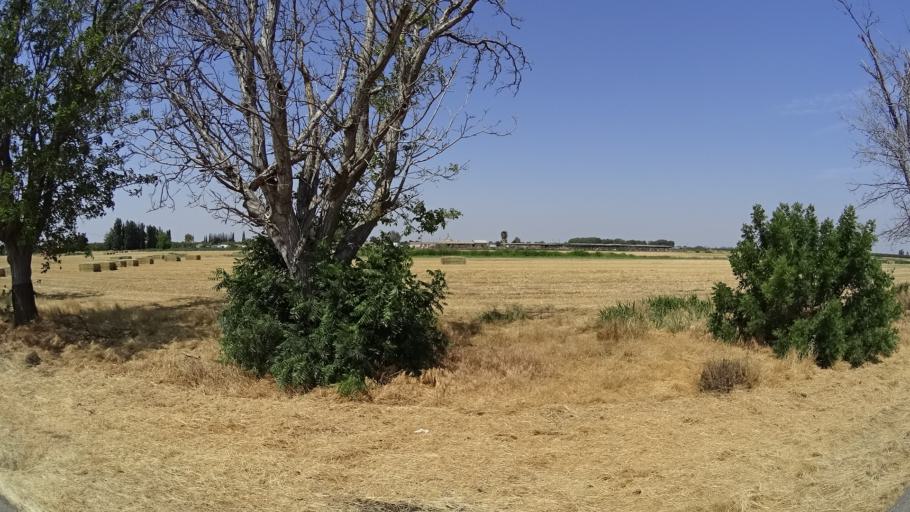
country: US
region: California
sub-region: Kings County
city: Armona
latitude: 36.3158
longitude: -119.7448
